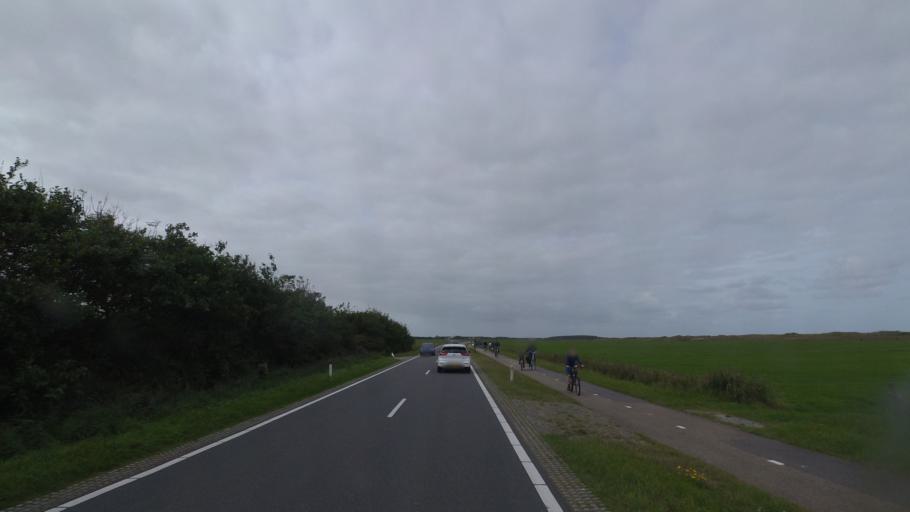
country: NL
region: Friesland
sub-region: Gemeente Ameland
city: Nes
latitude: 53.4458
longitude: 5.7456
